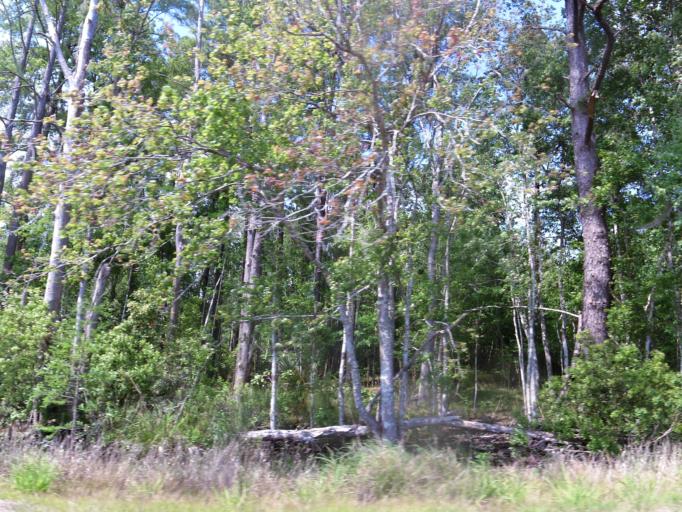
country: US
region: Georgia
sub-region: Camden County
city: Kingsland
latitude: 30.8104
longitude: -81.7766
